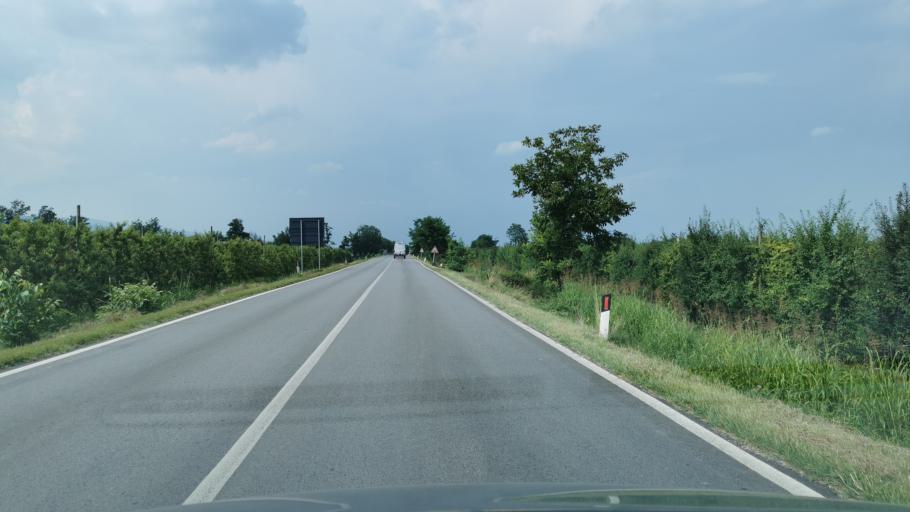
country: IT
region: Piedmont
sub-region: Provincia di Cuneo
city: Roata Rossi
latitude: 44.4630
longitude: 7.5385
